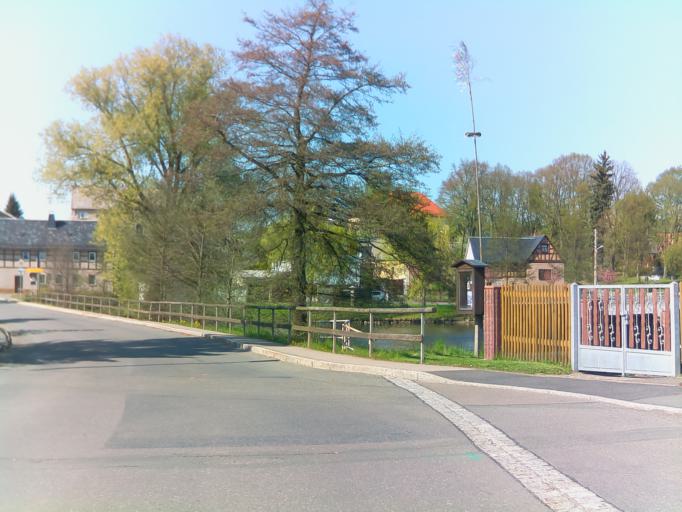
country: DE
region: Saxony
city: Pausa
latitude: 50.6238
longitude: 12.0365
